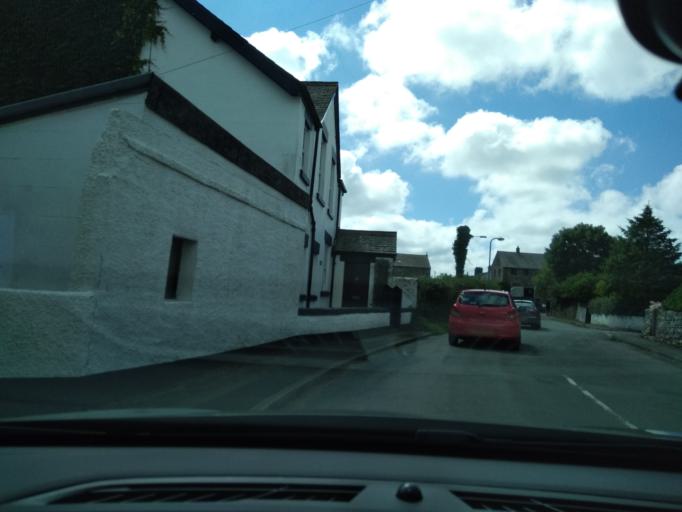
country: GB
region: England
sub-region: Cumbria
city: Millom
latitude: 54.2252
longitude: -3.3350
